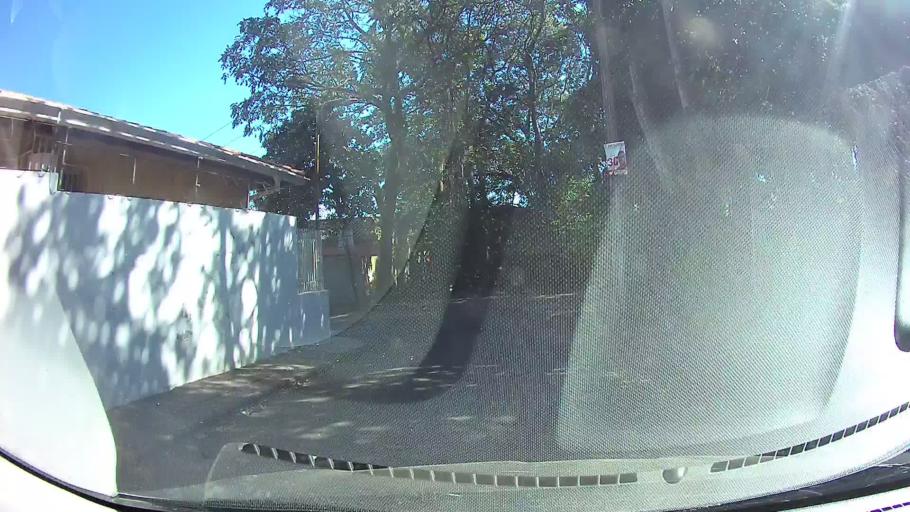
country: PY
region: Central
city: Villa Elisa
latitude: -25.3499
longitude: -57.5778
